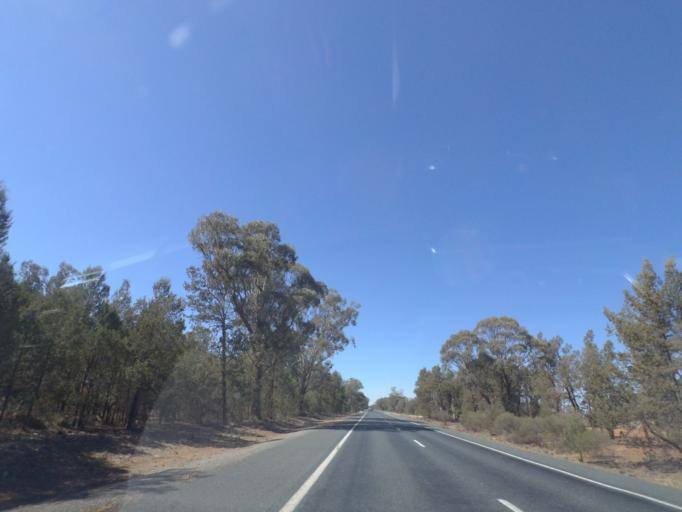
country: AU
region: New South Wales
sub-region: Bland
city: West Wyalong
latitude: -34.2134
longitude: 147.1082
